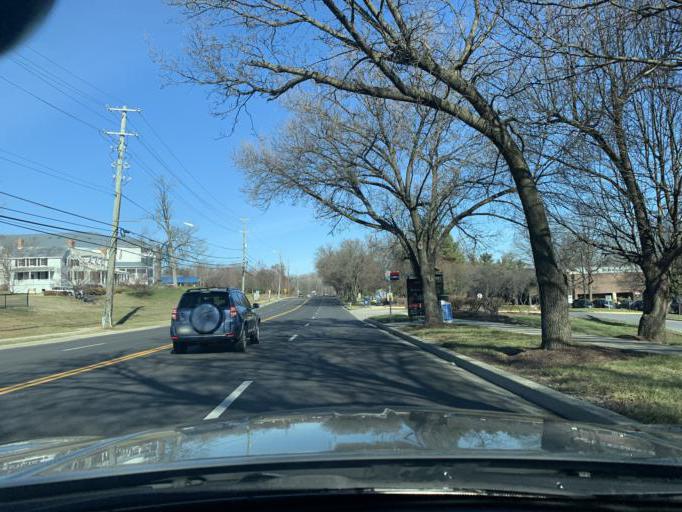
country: US
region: Maryland
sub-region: Prince George's County
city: Largo
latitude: 38.9019
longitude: -76.8532
